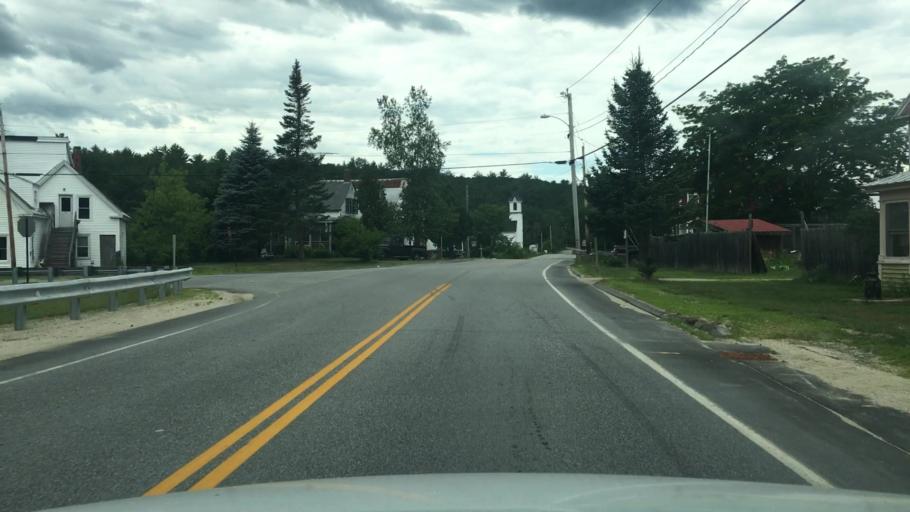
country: US
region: Maine
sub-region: Oxford County
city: Hartford
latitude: 44.3565
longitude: -70.3760
